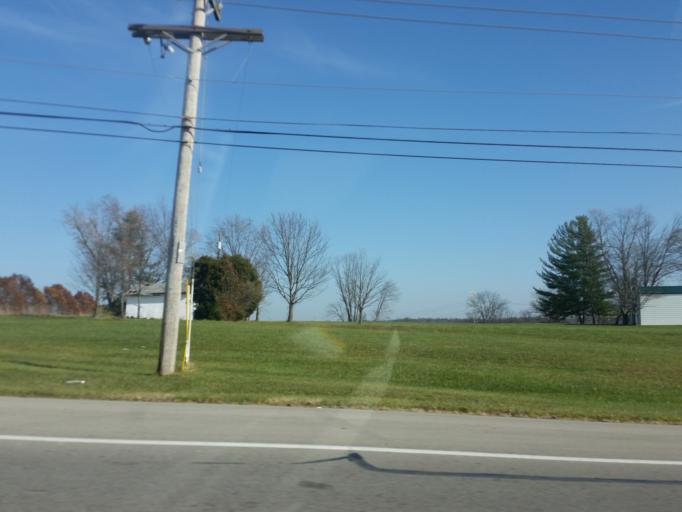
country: US
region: Ohio
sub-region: Butler County
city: Ross
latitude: 39.4033
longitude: -84.6656
